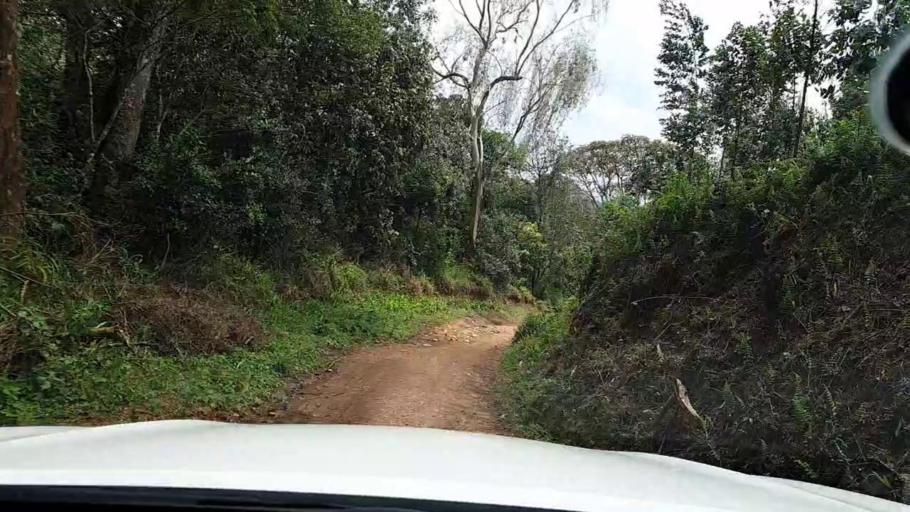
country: RW
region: Western Province
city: Kibuye
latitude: -2.2818
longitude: 29.3050
